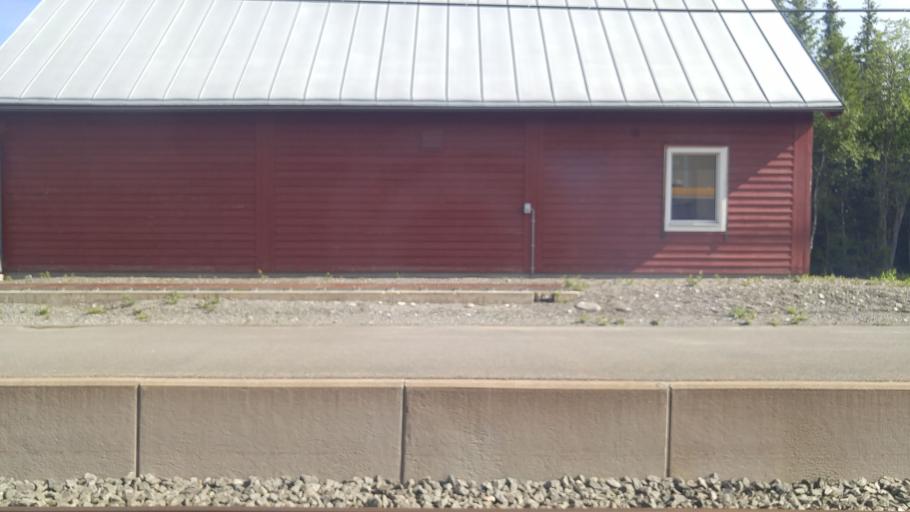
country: NO
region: Nord-Trondelag
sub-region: Meraker
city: Meraker
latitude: 63.2898
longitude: 12.3370
